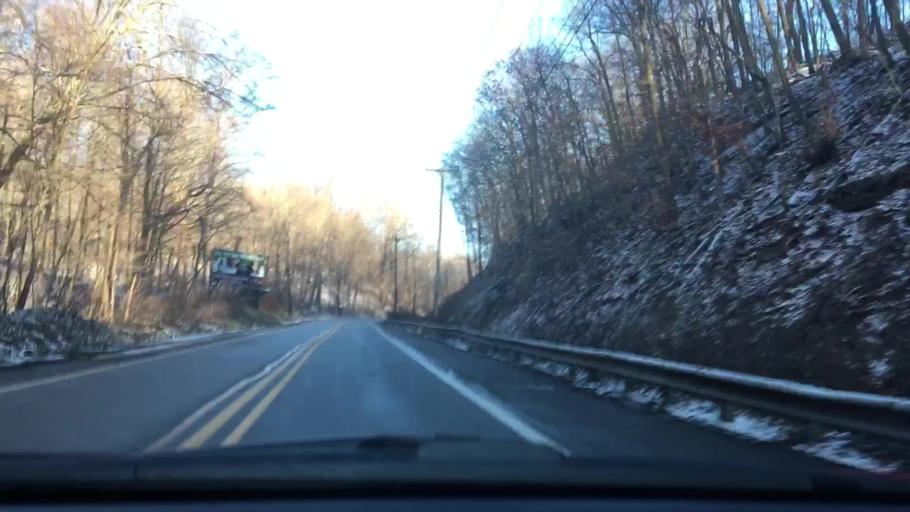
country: US
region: Pennsylvania
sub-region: Allegheny County
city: Glassport
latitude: 40.3309
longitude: -79.9102
